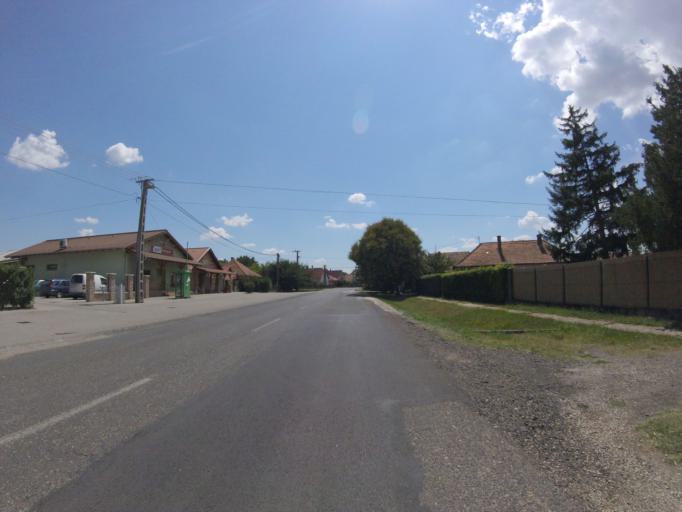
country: HU
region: Fejer
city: Ivancsa
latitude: 47.1588
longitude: 18.8280
